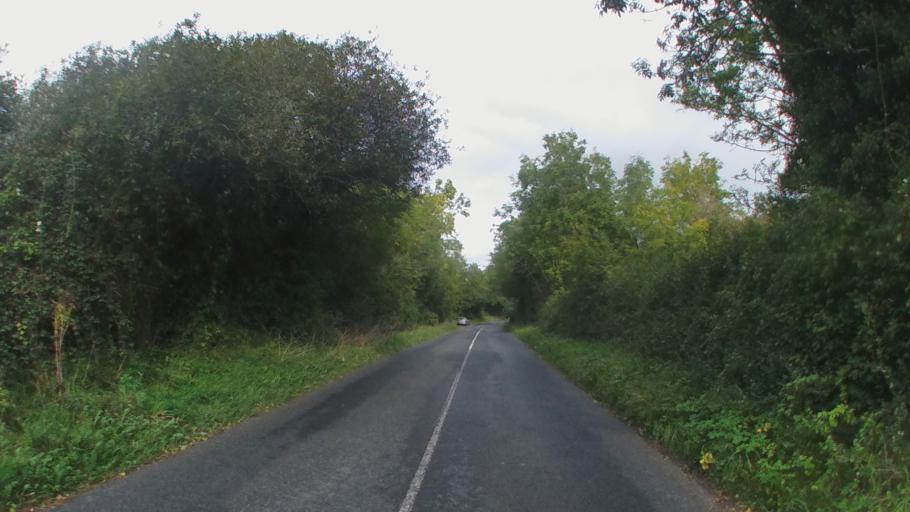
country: IE
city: Knocklyon
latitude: 53.2683
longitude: -6.3272
